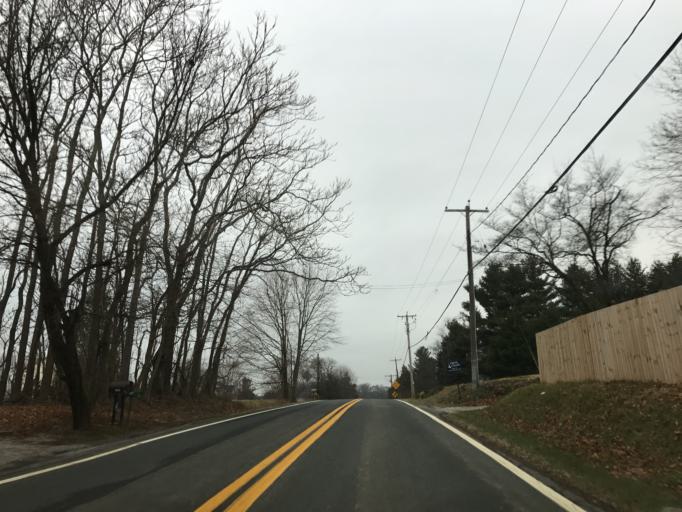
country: US
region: Maryland
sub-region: Carroll County
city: Westminster
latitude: 39.5266
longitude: -77.0305
